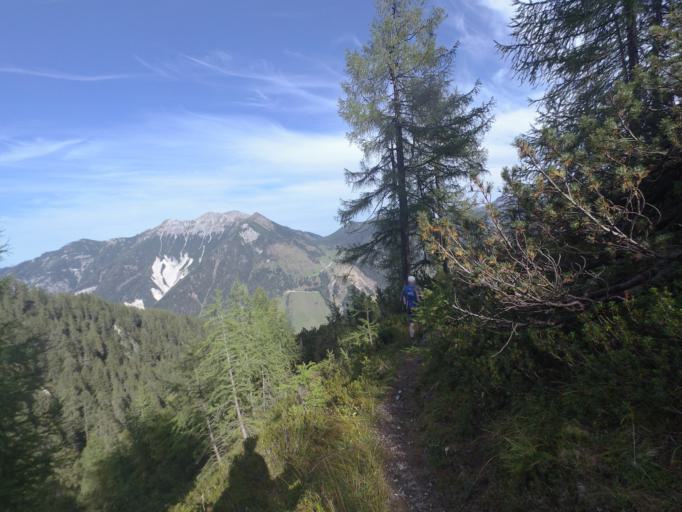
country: AT
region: Salzburg
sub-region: Politischer Bezirk Sankt Johann im Pongau
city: Kleinarl
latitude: 47.2391
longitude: 13.4098
